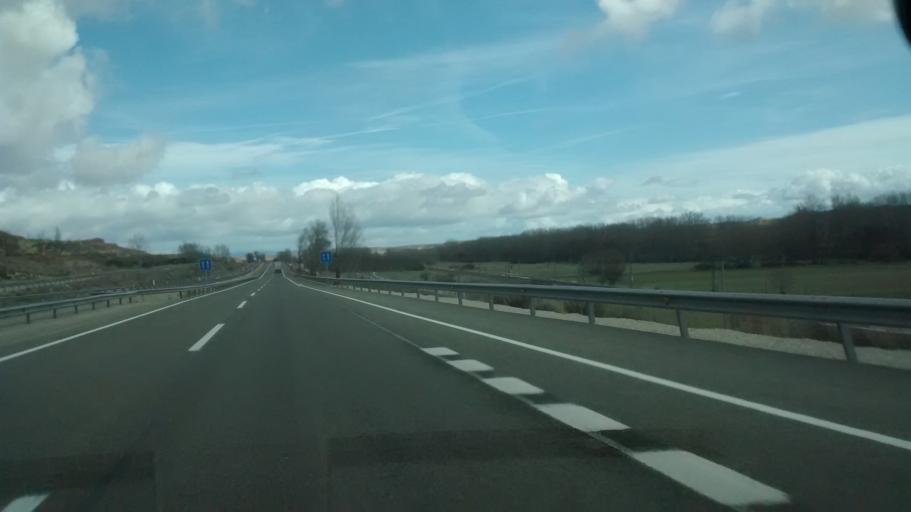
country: ES
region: Castille and Leon
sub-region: Provincia de Soria
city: Arcos de Jalon
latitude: 41.2264
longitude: -2.2546
